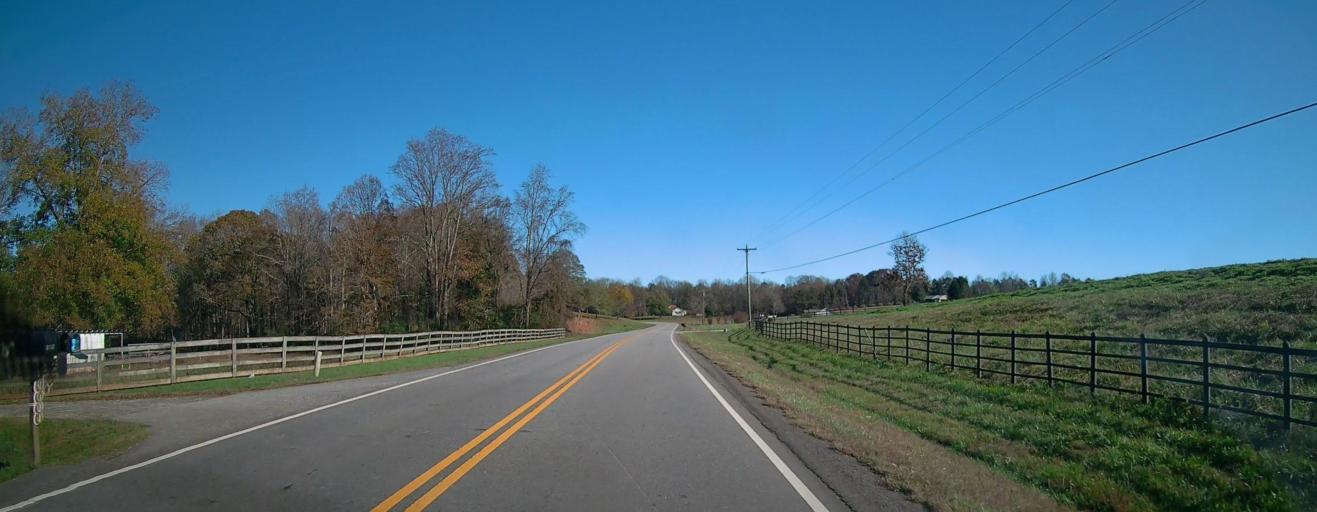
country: US
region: Georgia
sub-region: Hall County
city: Lula
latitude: 34.4737
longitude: -83.7438
